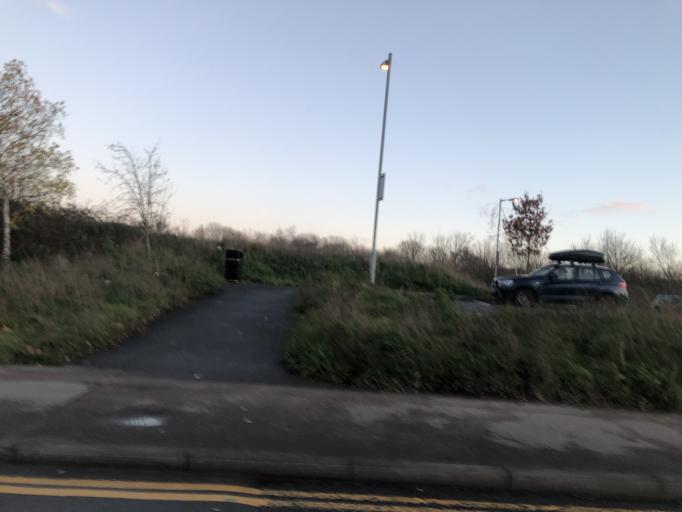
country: GB
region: England
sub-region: Greater London
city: Woolwich
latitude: 51.4783
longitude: 0.0520
